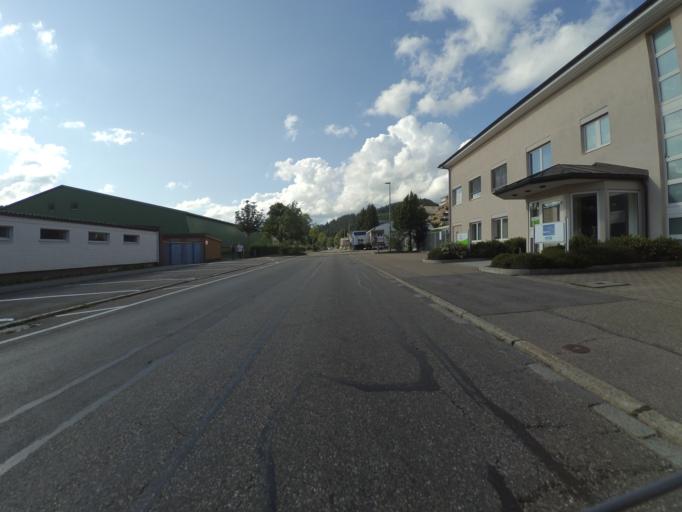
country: DE
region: Baden-Wuerttemberg
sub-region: Freiburg Region
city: Titisee-Neustadt
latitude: 47.9188
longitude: 8.2037
